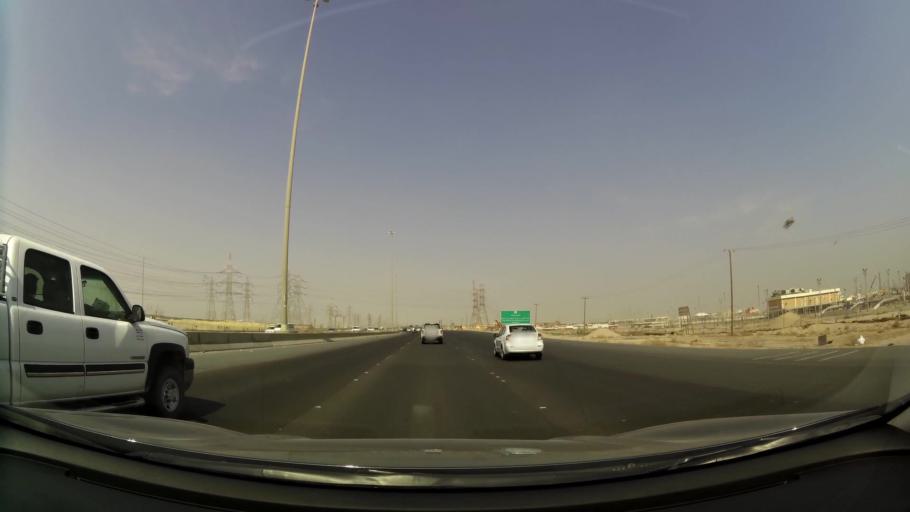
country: KW
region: Al Ahmadi
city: Al Fahahil
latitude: 29.0524
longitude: 48.1113
